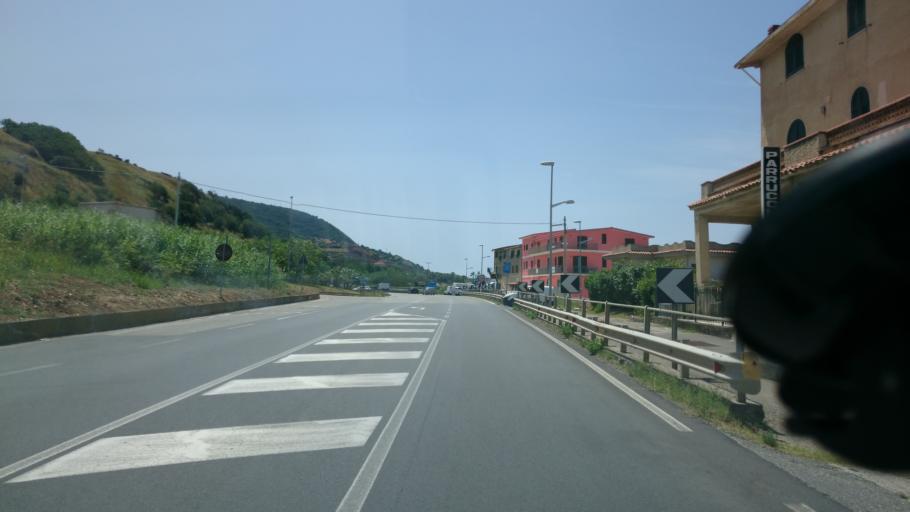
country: IT
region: Calabria
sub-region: Provincia di Cosenza
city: Cittadella del Capo
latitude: 39.5695
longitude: 15.8728
